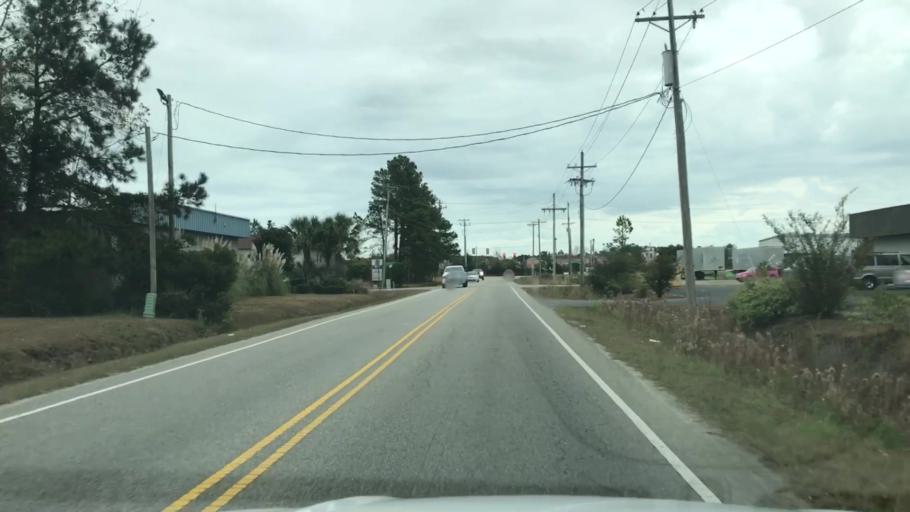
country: US
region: South Carolina
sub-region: Horry County
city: Forestbrook
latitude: 33.7154
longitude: -78.9390
